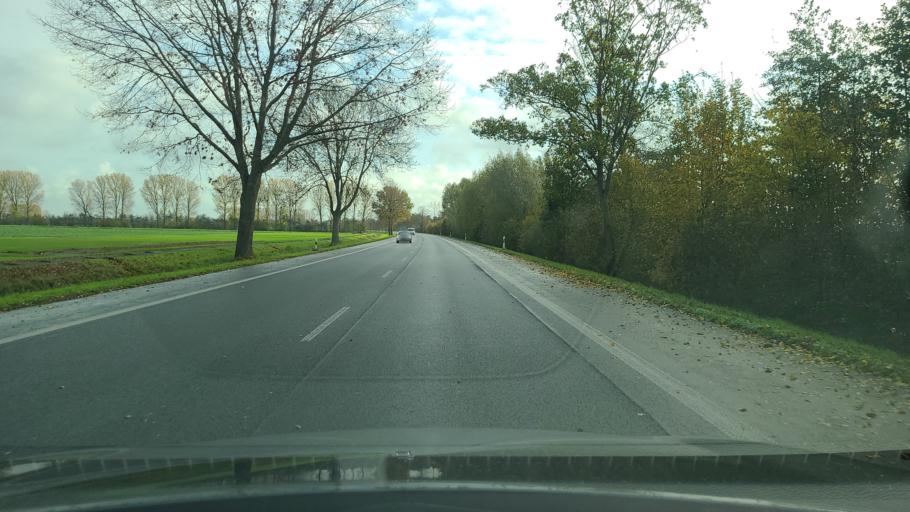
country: NL
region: Gelderland
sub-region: Gemeente Groesbeek
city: De Horst
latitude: 51.8030
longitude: 5.9857
